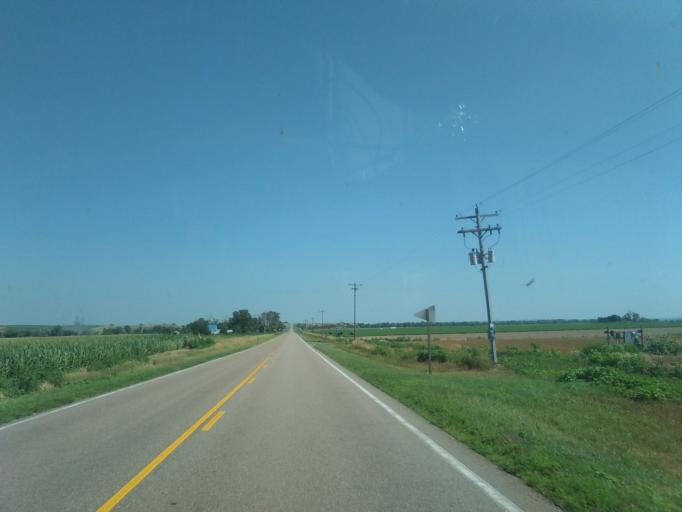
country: US
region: Nebraska
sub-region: Dundy County
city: Benkelman
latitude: 39.9946
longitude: -101.5421
